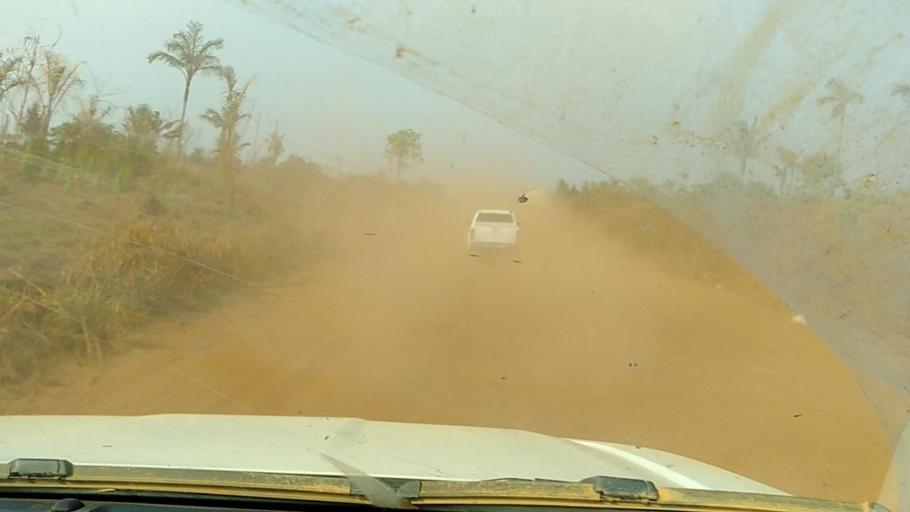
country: BR
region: Rondonia
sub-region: Porto Velho
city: Porto Velho
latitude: -8.7345
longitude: -63.9664
